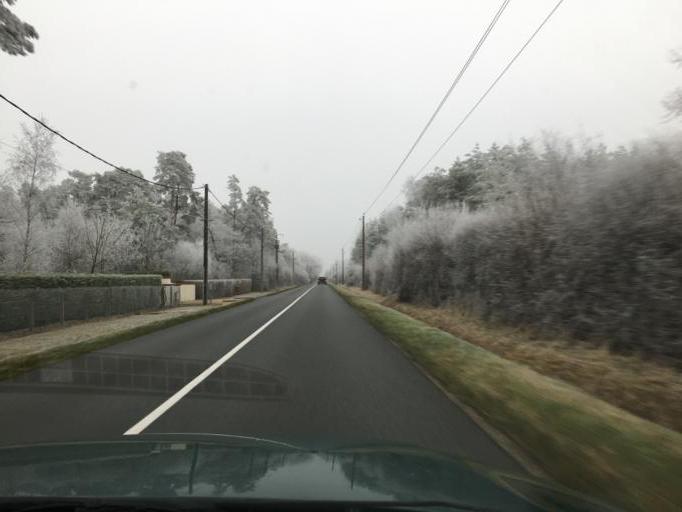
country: FR
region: Centre
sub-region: Departement du Loiret
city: Jouy-le-Potier
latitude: 47.7169
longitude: 1.7972
